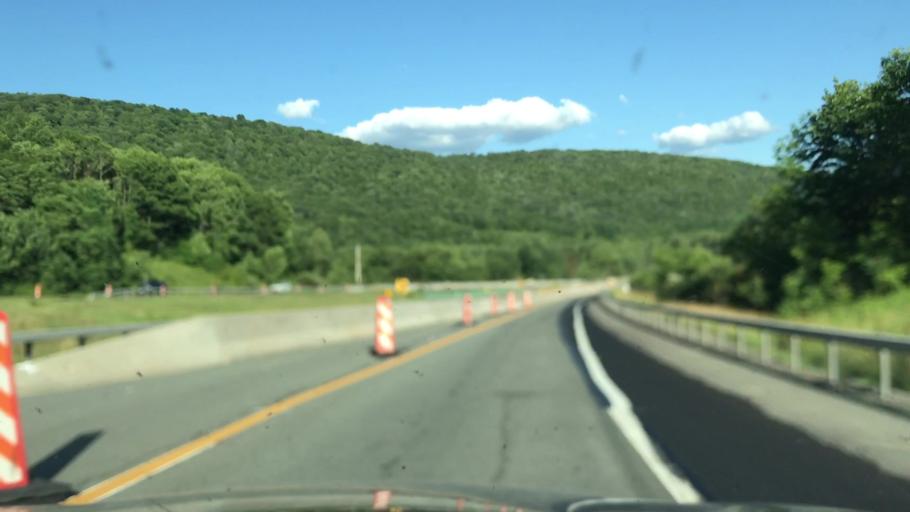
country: US
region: New York
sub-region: Sullivan County
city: Livingston Manor
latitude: 41.9567
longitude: -74.9384
